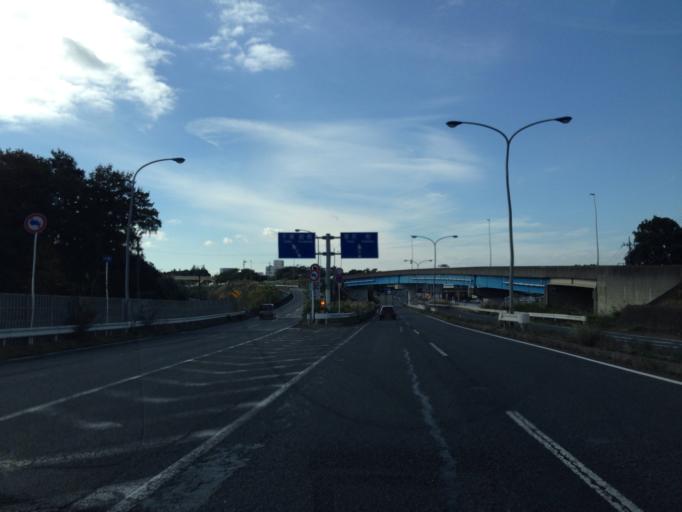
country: JP
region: Chiba
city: Abiko
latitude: 35.8785
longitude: 140.0348
